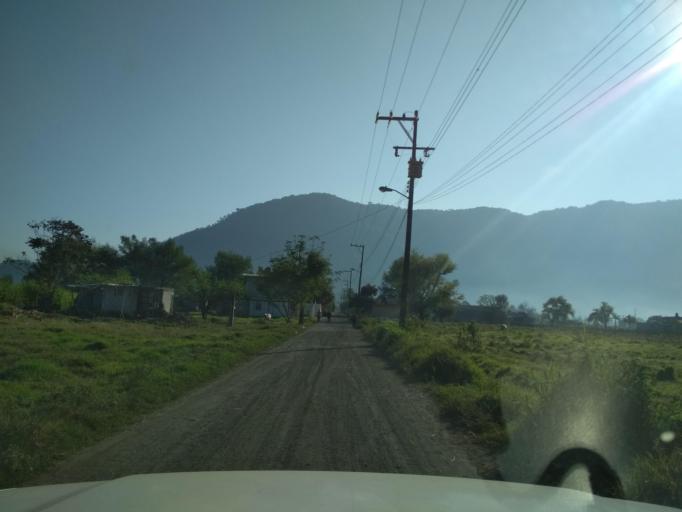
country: MX
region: Veracruz
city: Jalapilla
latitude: 18.8243
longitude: -97.0810
